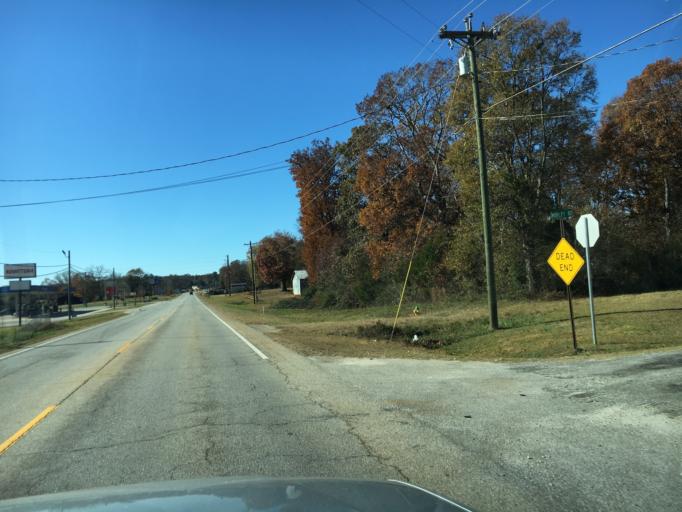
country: US
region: Georgia
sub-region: Hart County
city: Hartwell
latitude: 34.3475
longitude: -82.8864
